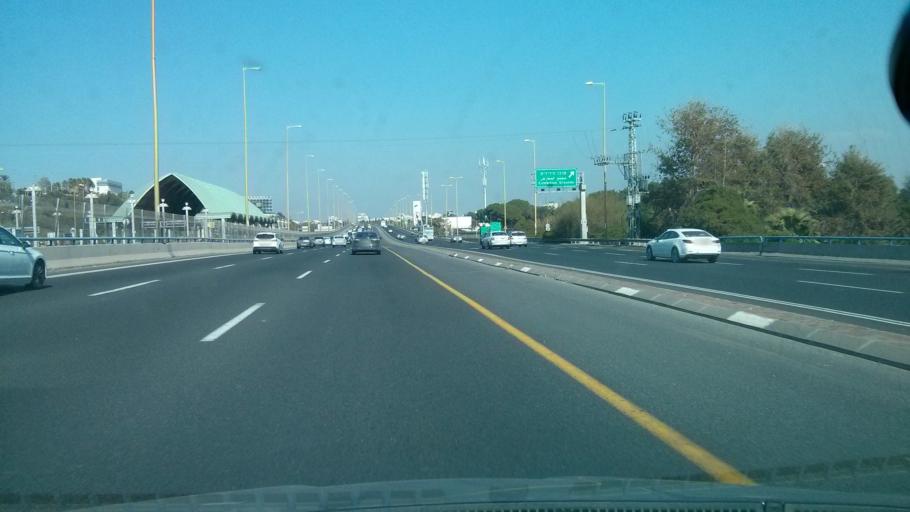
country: IL
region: Tel Aviv
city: Ramat Gan
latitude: 32.1022
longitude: 34.8040
